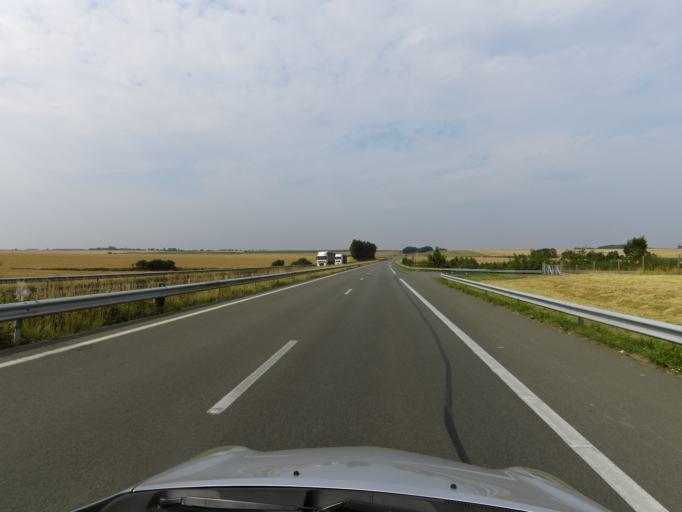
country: FR
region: Picardie
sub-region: Departement de la Somme
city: Epehy
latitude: 50.0213
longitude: 3.1707
